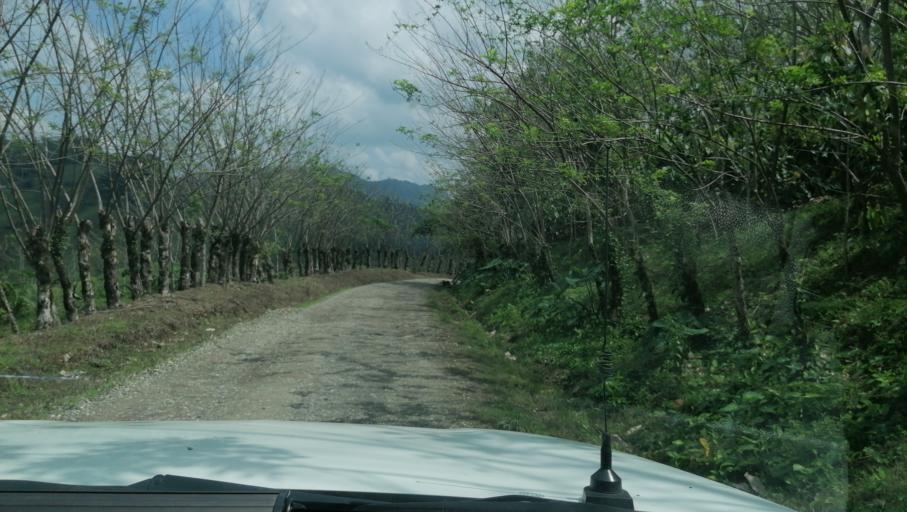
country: MX
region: Chiapas
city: Ixtacomitan
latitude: 17.4397
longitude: -93.2040
